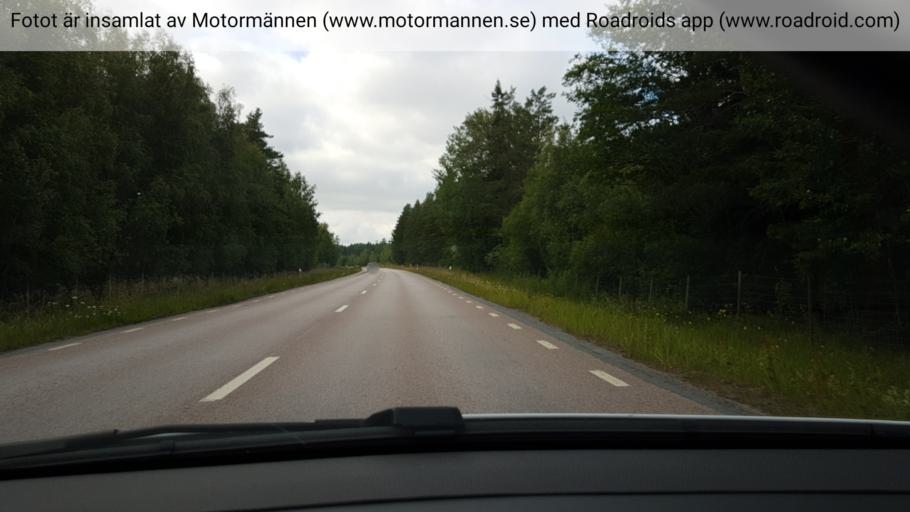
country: SE
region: Uppsala
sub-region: Osthammars Kommun
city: Osterbybruk
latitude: 60.4121
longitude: 17.8666
